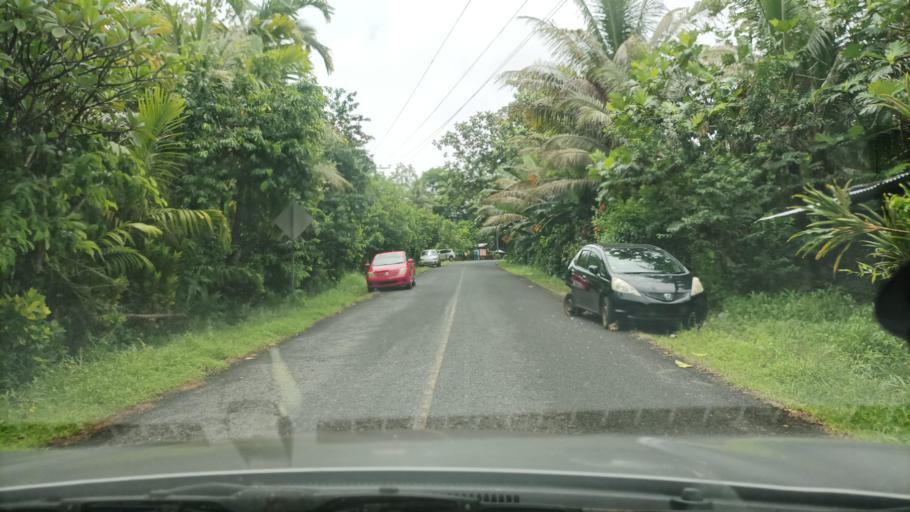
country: FM
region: Pohnpei
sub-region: Madolenihm Municipality
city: Madolenihm Municipality Government
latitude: 6.8706
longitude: 158.2869
